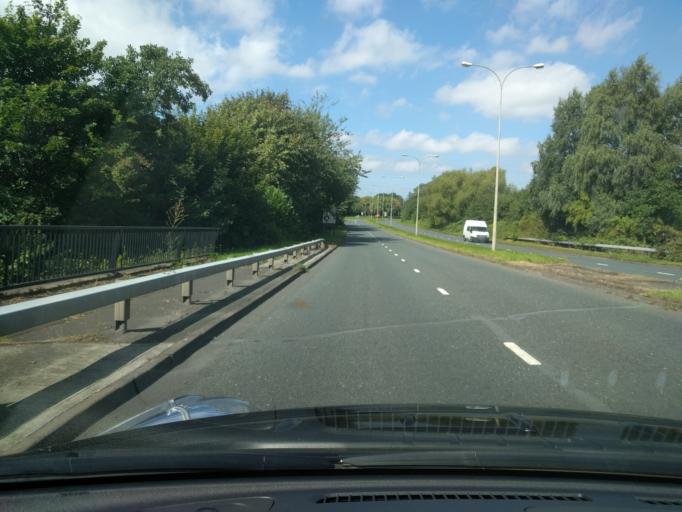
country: GB
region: England
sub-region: Warrington
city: Croft
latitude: 53.4110
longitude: -2.5367
